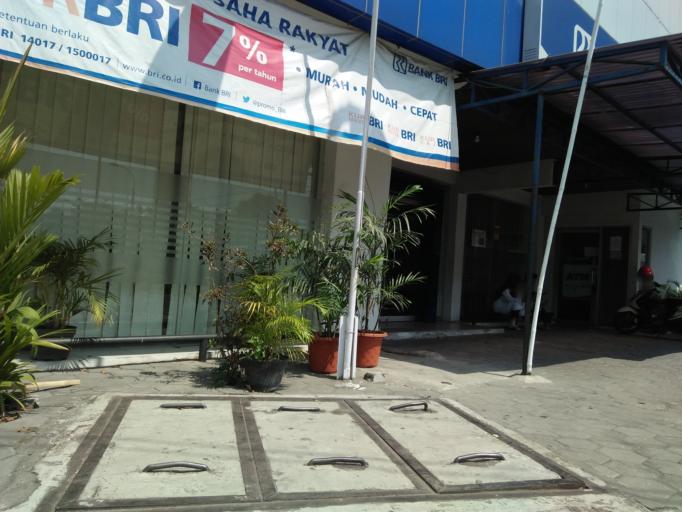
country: ID
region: Daerah Istimewa Yogyakarta
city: Kasihan
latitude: -7.8131
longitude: 110.3563
